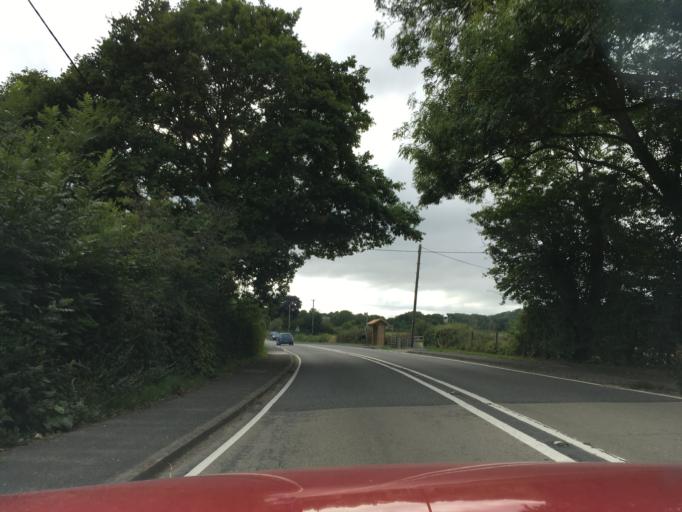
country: GB
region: England
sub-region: Hampshire
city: Petersfield
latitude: 51.0085
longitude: -0.9662
